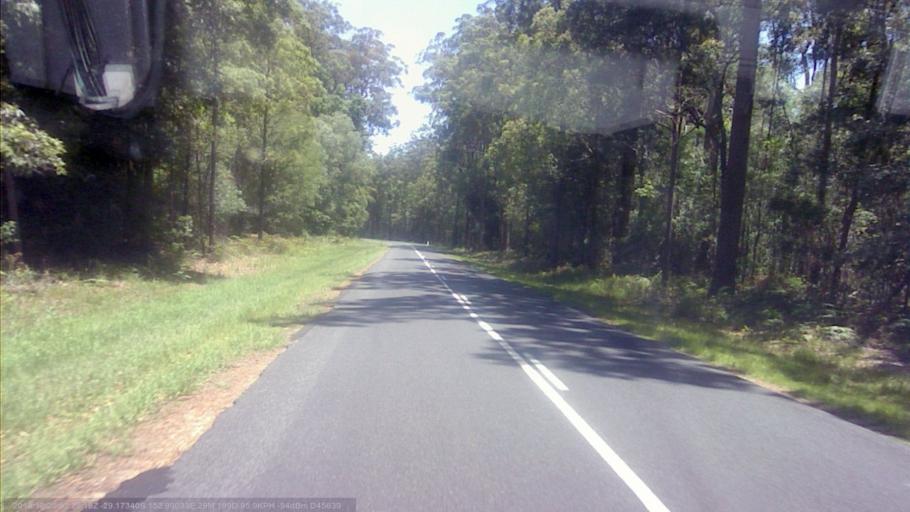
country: AU
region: New South Wales
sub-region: Clarence Valley
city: Gordon
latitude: -29.1734
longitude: 152.9903
